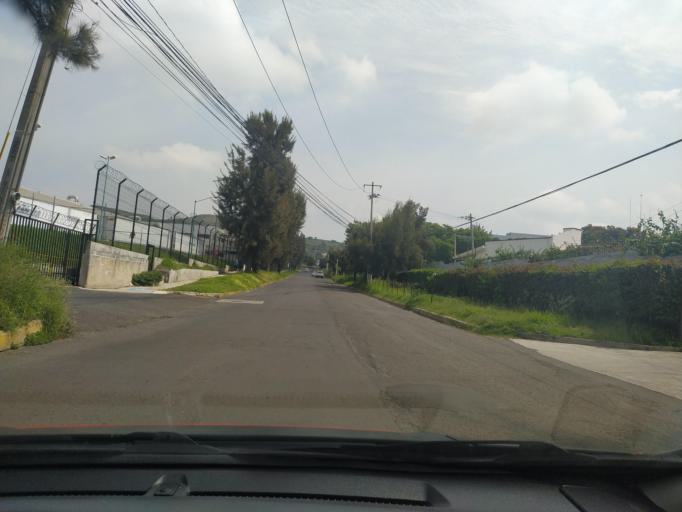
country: MX
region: Jalisco
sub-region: Tlajomulco de Zuniga
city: La Tijera
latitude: 20.6049
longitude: -103.4060
